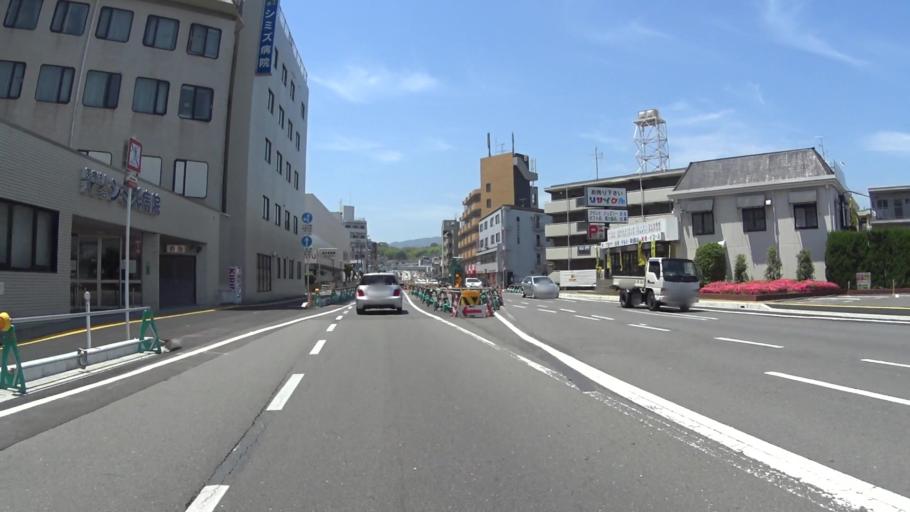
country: JP
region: Kyoto
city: Muko
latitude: 34.9817
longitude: 135.6925
